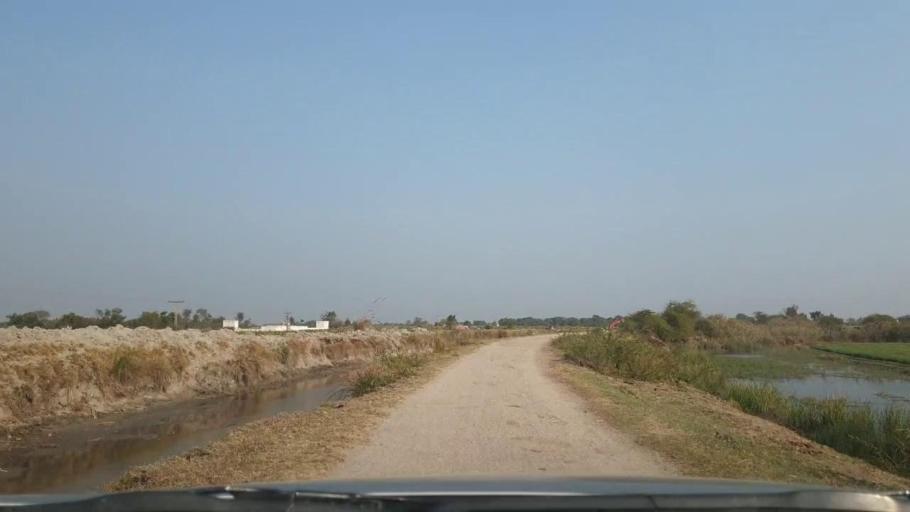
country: PK
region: Sindh
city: Tando Adam
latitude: 25.6501
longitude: 68.5908
